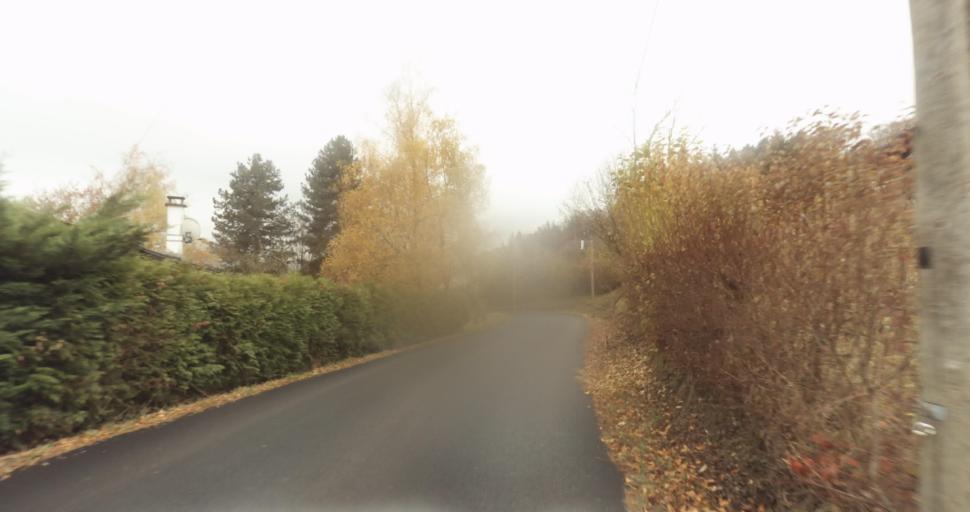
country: FR
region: Rhone-Alpes
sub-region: Departement de la Haute-Savoie
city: Saint-Martin-Bellevue
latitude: 45.9837
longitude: 6.1532
